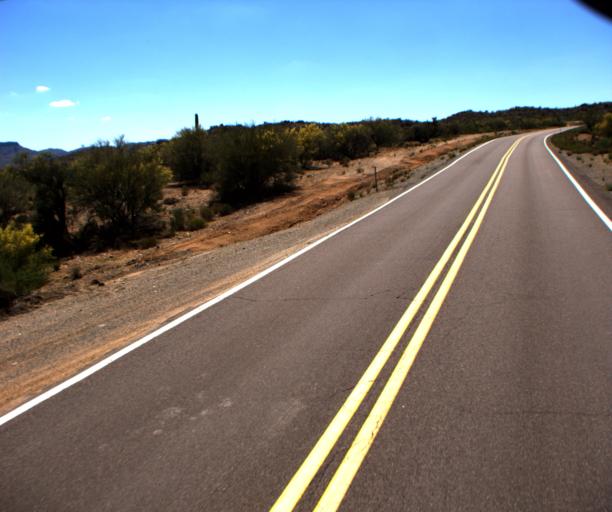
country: US
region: Arizona
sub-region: Yavapai County
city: Bagdad
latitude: 34.4606
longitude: -113.2402
